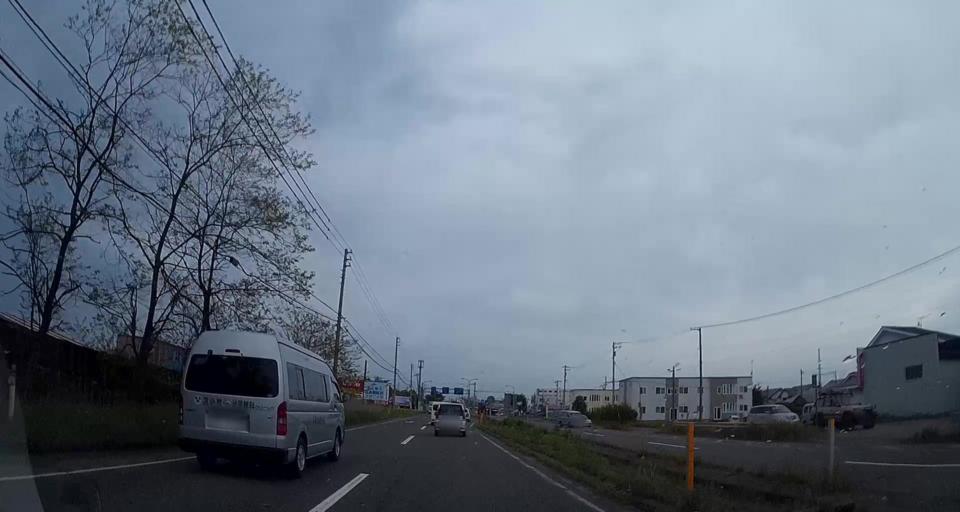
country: JP
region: Hokkaido
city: Tomakomai
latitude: 42.6706
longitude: 141.7011
